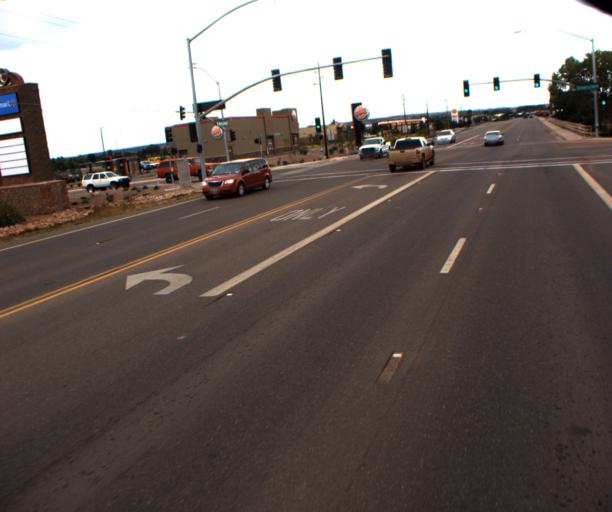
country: US
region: Arizona
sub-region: Navajo County
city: Taylor
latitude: 34.4755
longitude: -110.0866
